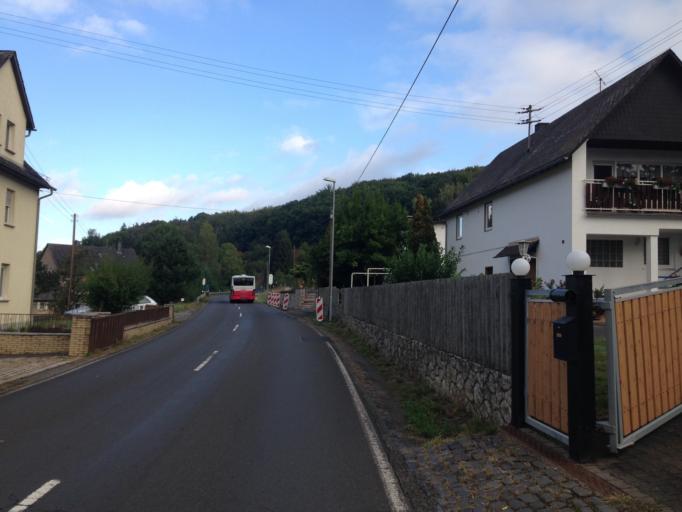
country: DE
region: Hesse
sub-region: Regierungsbezirk Giessen
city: Heuchelheim
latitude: 50.6322
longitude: 8.5735
